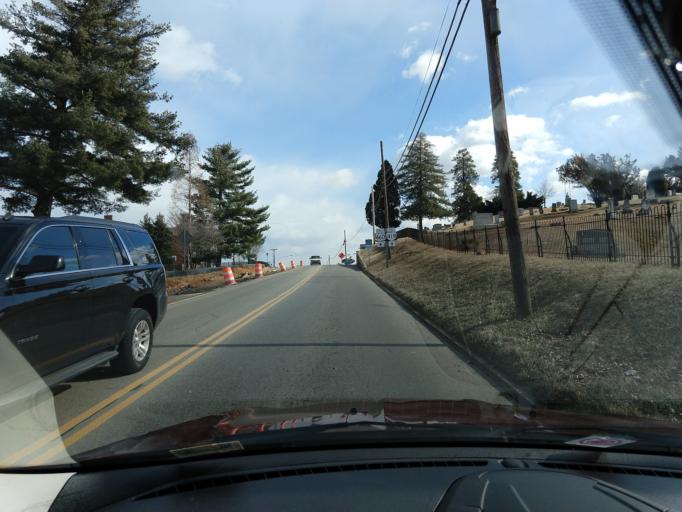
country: US
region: Virginia
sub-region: City of Salem
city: Salem
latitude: 37.2943
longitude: -80.0487
